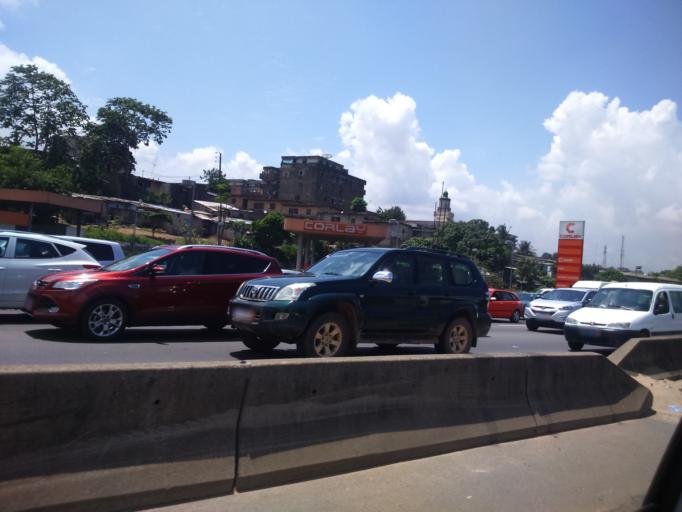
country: CI
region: Lagunes
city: Abidjan
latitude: 5.3621
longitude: -4.0234
